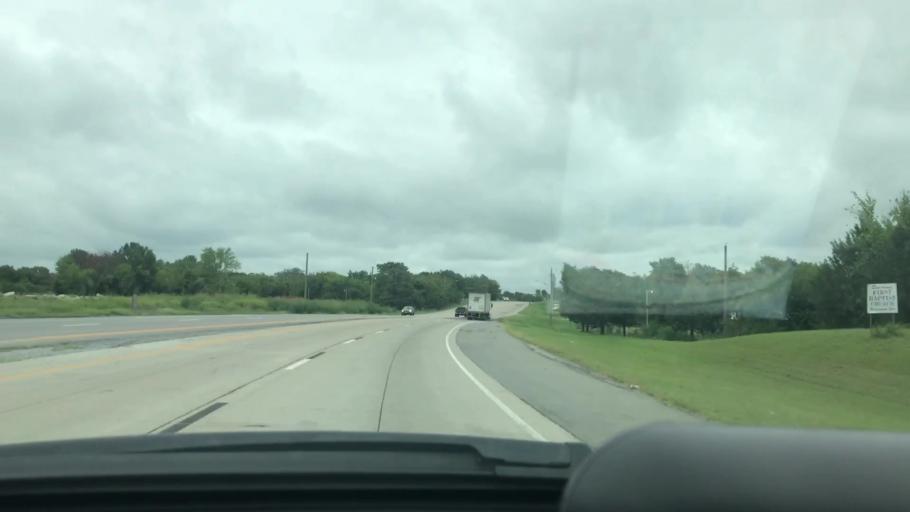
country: US
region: Oklahoma
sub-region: Pittsburg County
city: McAlester
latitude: 34.8224
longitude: -95.8501
